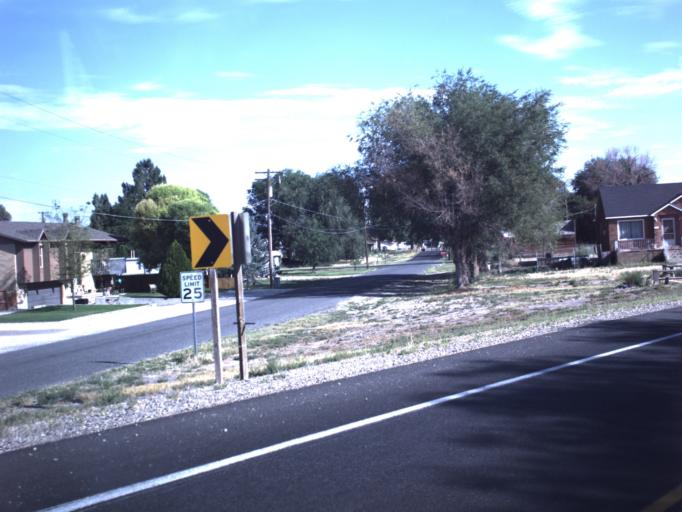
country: US
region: Utah
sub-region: Sevier County
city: Salina
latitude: 39.0062
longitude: -111.8616
